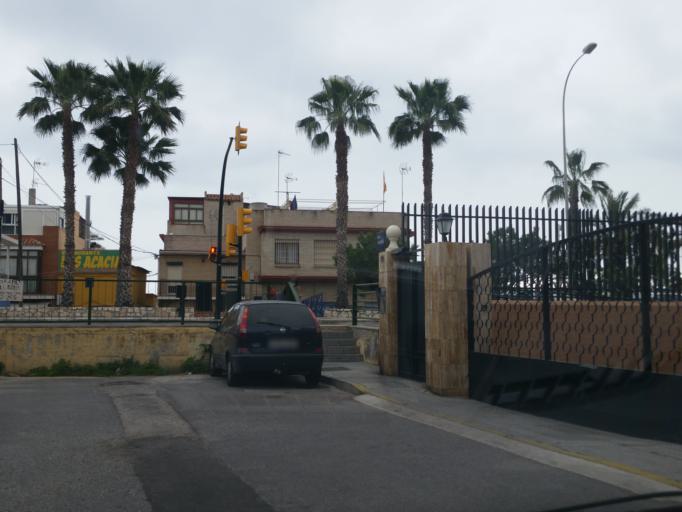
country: ES
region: Andalusia
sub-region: Provincia de Malaga
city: Malaga
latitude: 36.7203
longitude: -4.3678
